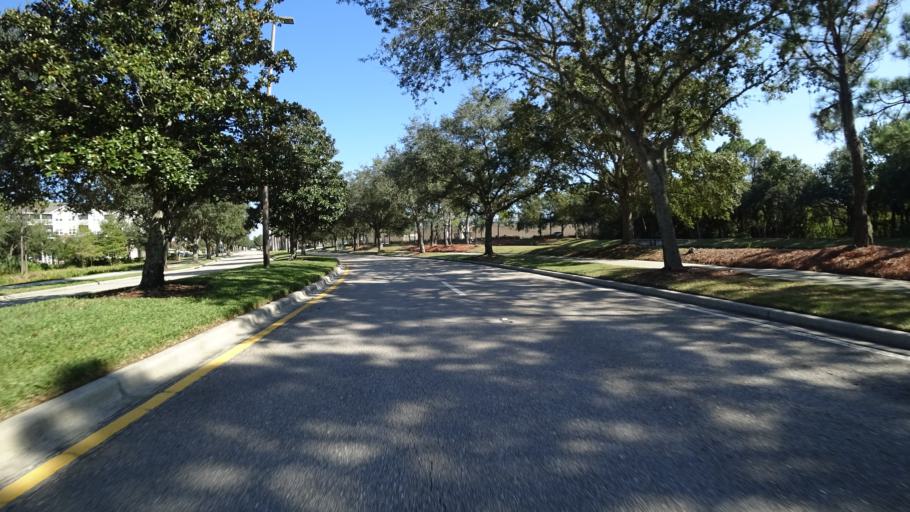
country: US
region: Florida
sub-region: Sarasota County
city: The Meadows
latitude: 27.3915
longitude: -82.4447
